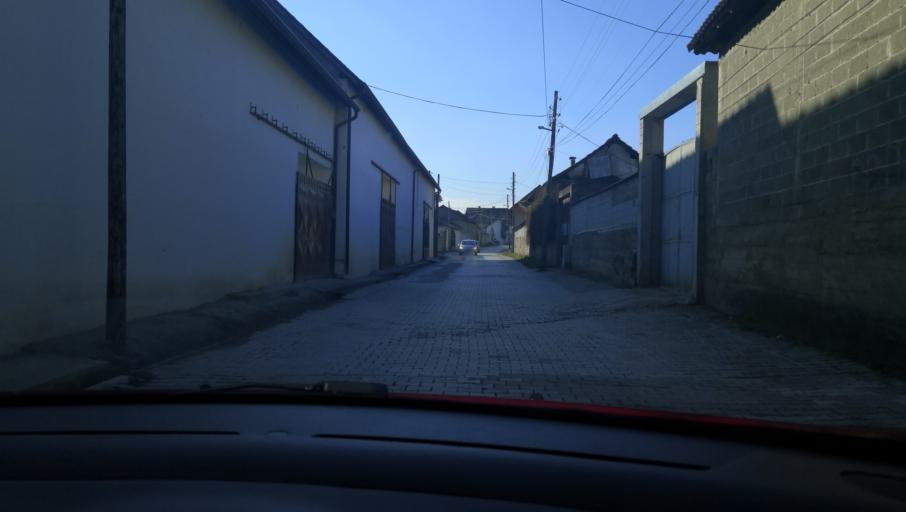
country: MK
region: Brvenica
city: Celopek
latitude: 41.9376
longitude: 21.0072
